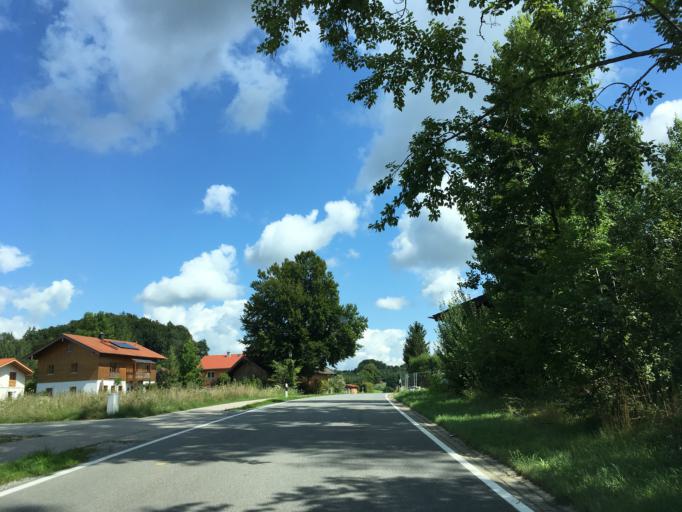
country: DE
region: Bavaria
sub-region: Upper Bavaria
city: Eggstatt
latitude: 47.9413
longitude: 12.3749
